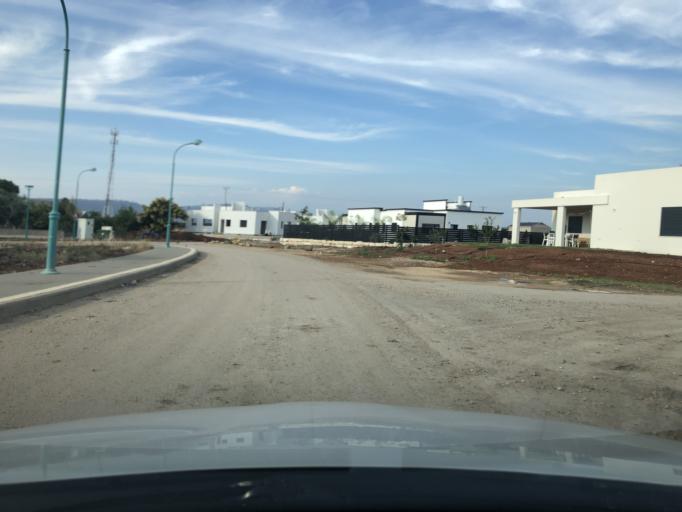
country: IL
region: Northern District
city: Yavne'el
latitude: 32.6624
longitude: 35.5864
